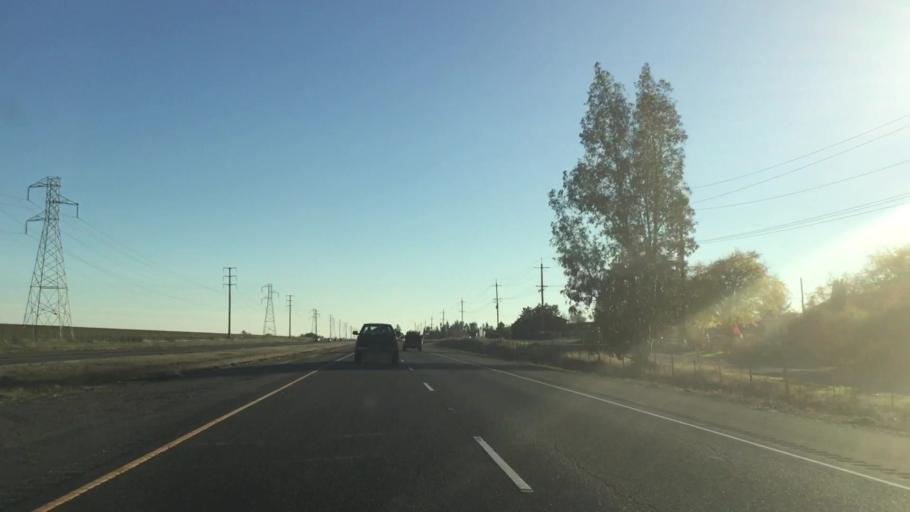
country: US
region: California
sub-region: Yuba County
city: Plumas Lake
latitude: 39.0438
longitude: -121.5433
